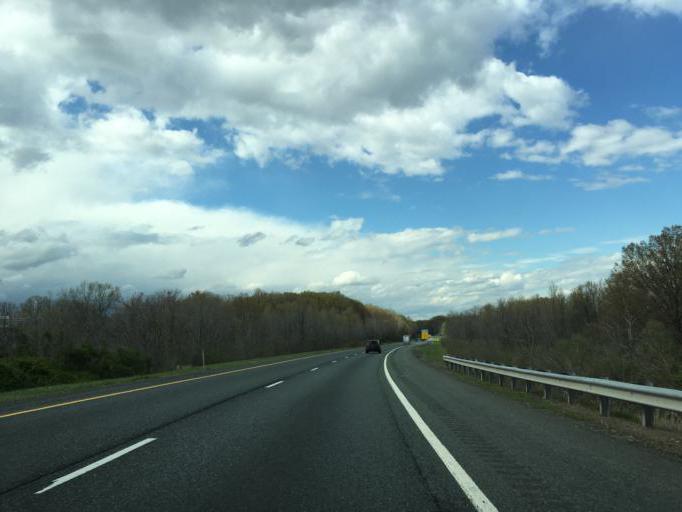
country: US
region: Maryland
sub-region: Baltimore County
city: Edgemere
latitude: 39.2541
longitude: -76.4574
